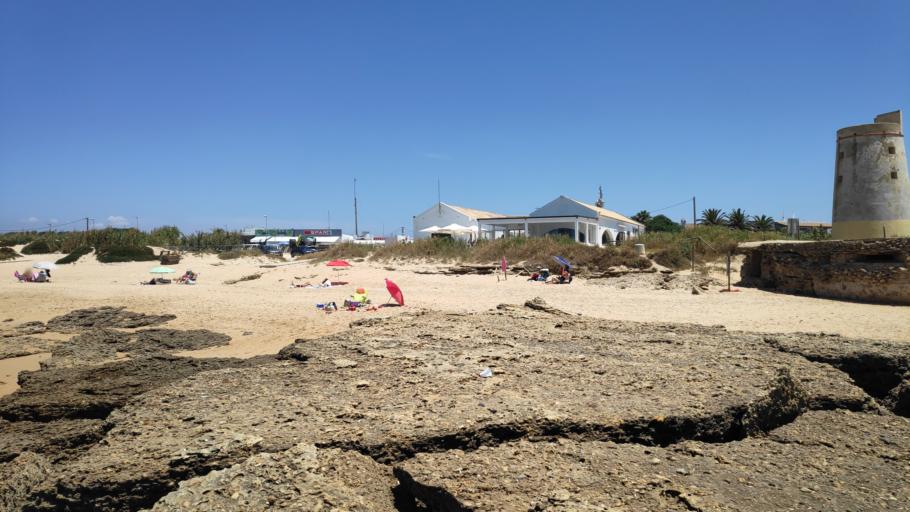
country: ES
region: Andalusia
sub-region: Provincia de Cadiz
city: Conil de la Frontera
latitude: 36.2321
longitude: -6.0722
